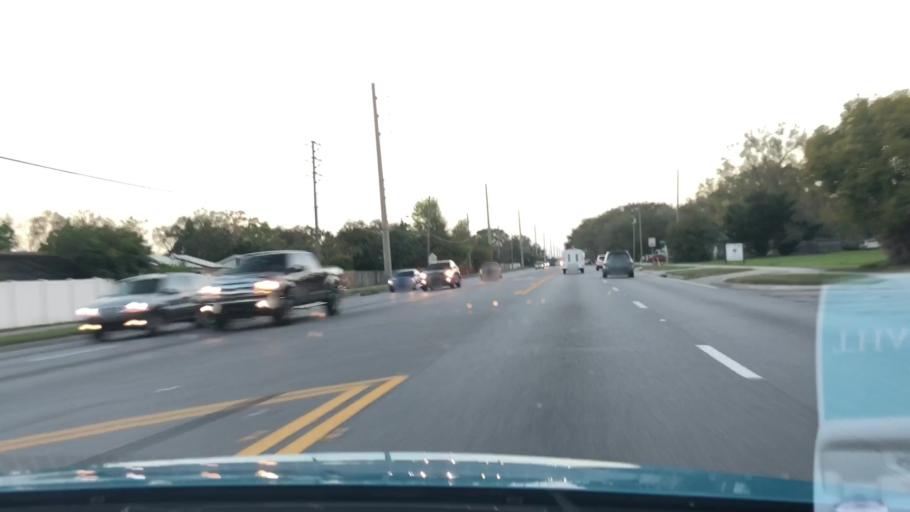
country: US
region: Florida
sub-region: Osceola County
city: Kissimmee
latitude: 28.3149
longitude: -81.3913
